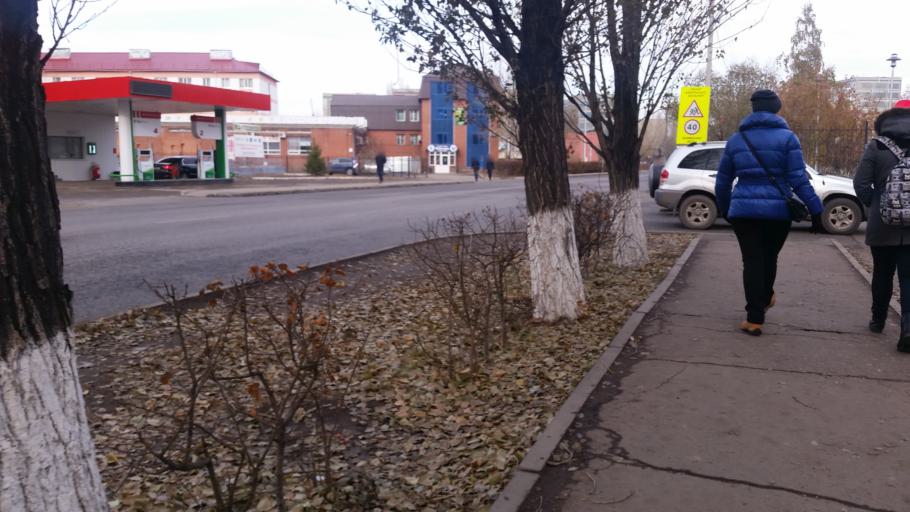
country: KZ
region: Astana Qalasy
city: Astana
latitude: 51.1521
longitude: 71.4744
